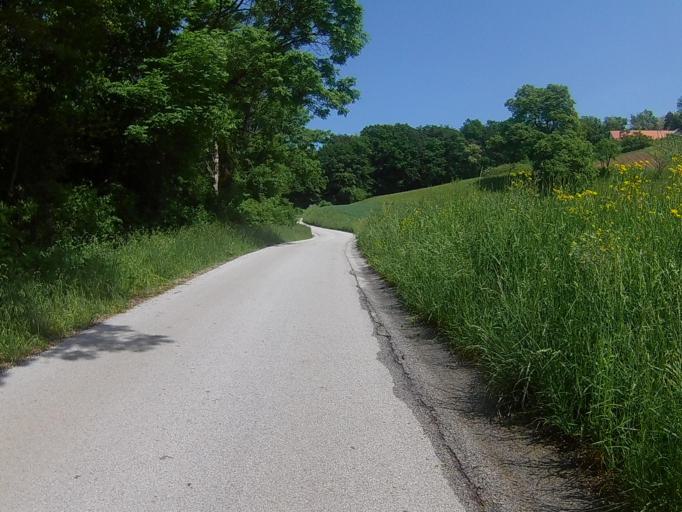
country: SI
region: Pesnica
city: Pesnica pri Mariboru
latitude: 46.5695
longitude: 15.7043
